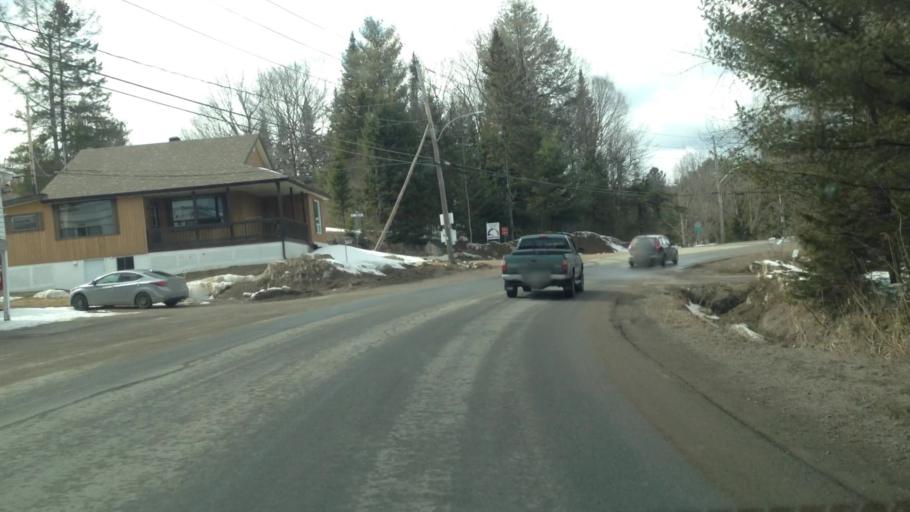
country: CA
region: Quebec
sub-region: Laurentides
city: Brownsburg-Chatham
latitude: 45.7284
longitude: -74.4845
